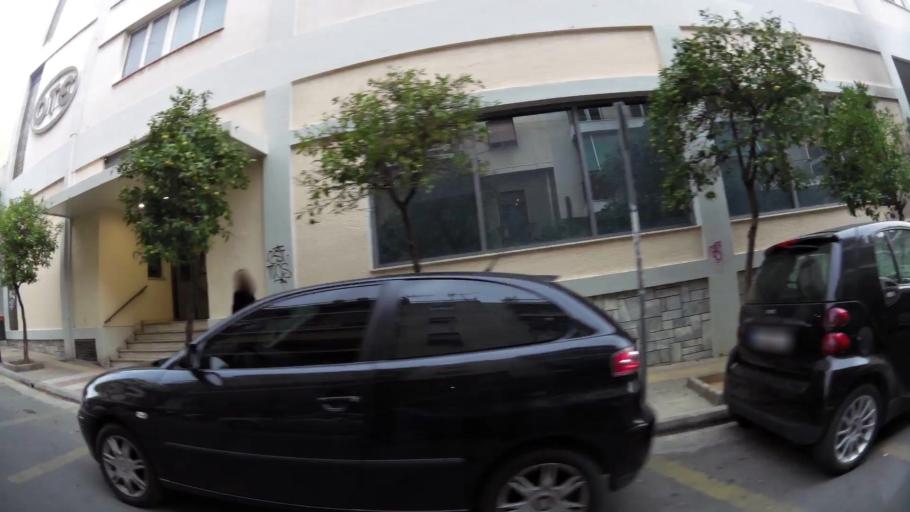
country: GR
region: Attica
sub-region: Nomos Attikis
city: Piraeus
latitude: 37.9341
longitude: 23.6410
